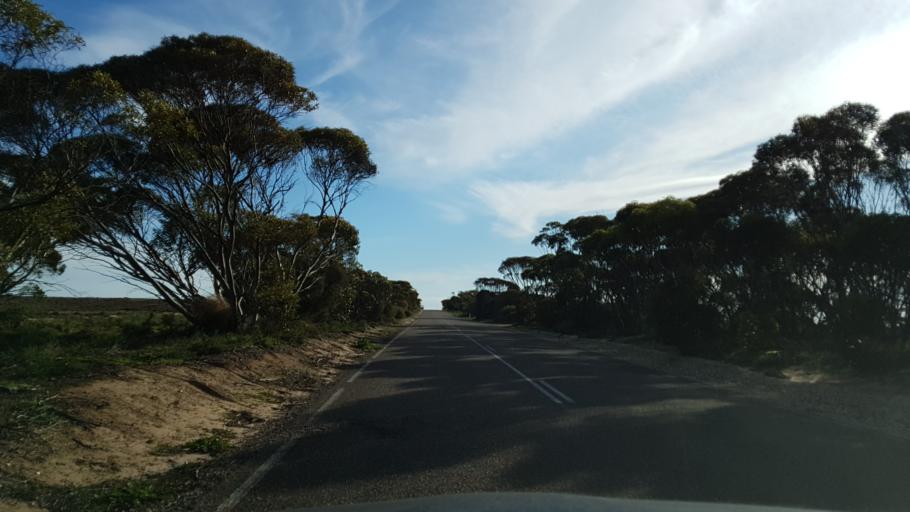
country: AU
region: South Australia
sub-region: Murray Bridge
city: Tailem Bend
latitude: -35.0644
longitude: 139.4652
